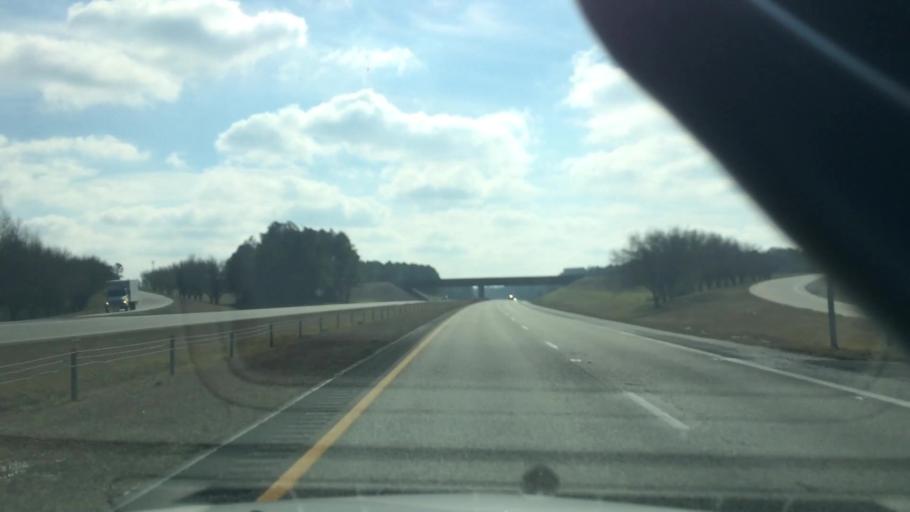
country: US
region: North Carolina
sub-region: Duplin County
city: Wallace
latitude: 34.6900
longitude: -77.9458
